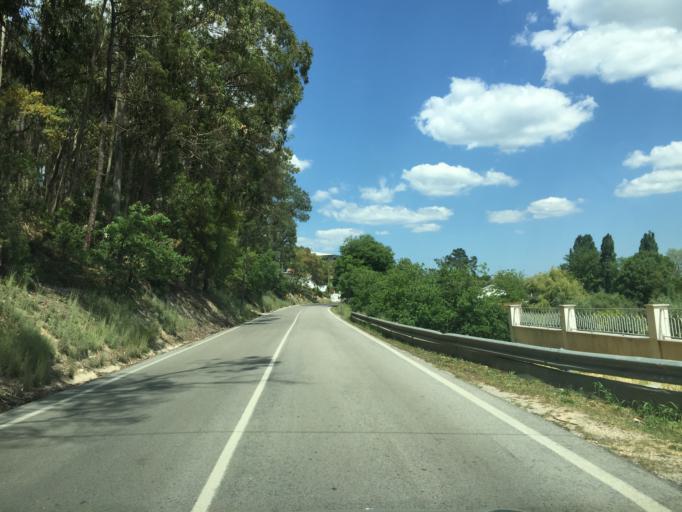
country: PT
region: Santarem
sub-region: Ourem
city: Ourem
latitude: 39.6541
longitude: -8.5999
